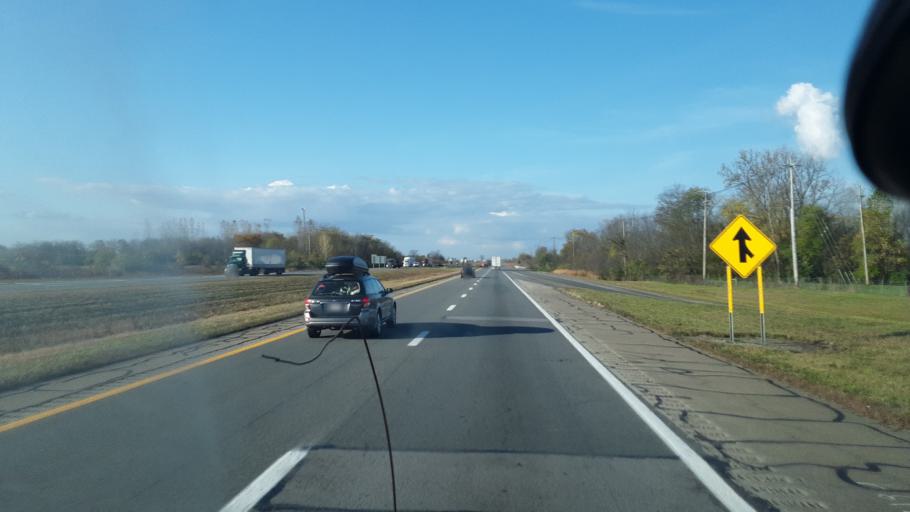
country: US
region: Ohio
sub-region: Madison County
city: Bethel
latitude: 39.6956
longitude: -83.4597
